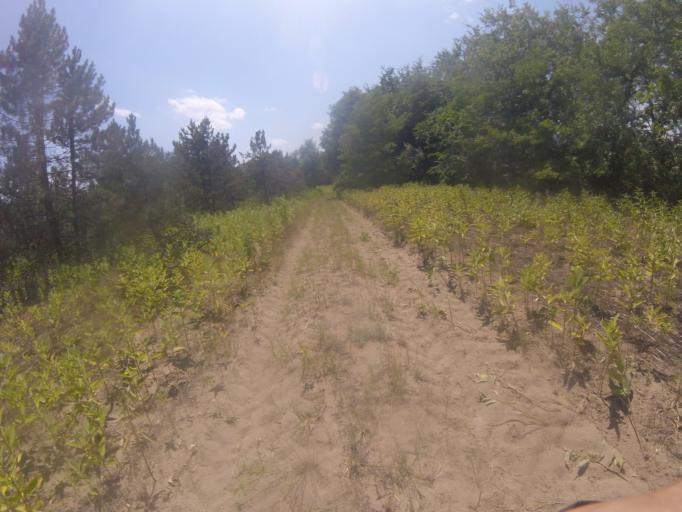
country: HU
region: Bacs-Kiskun
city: Jaszszentlaszlo
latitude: 46.6054
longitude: 19.7130
